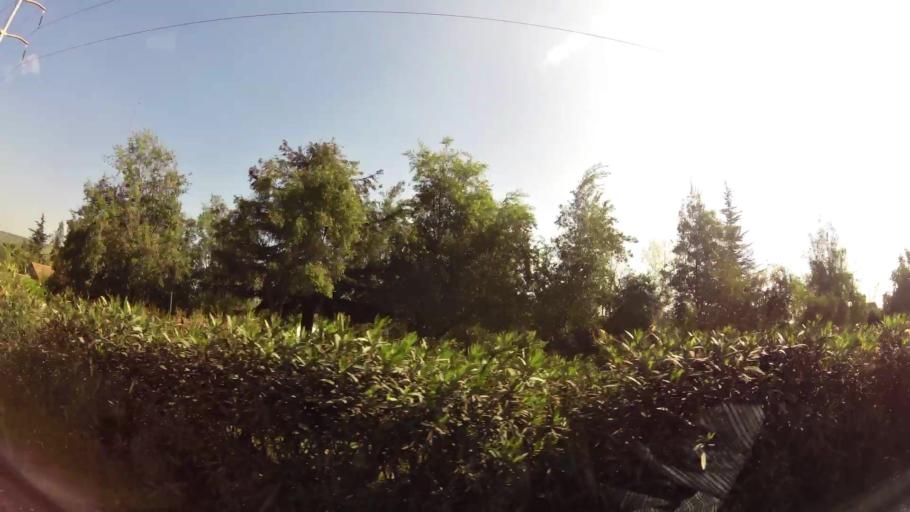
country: CL
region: Santiago Metropolitan
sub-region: Provincia de Santiago
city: Villa Presidente Frei, Nunoa, Santiago, Chile
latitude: -33.4082
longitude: -70.5148
